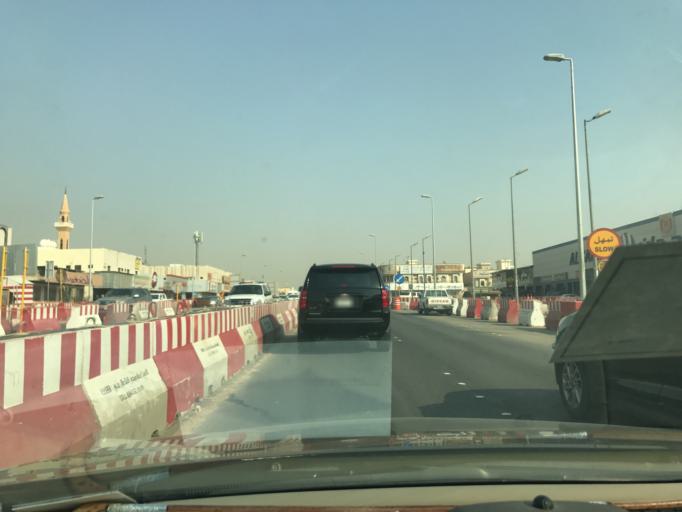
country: SA
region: Ar Riyad
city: Riyadh
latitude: 24.7532
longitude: 46.7701
